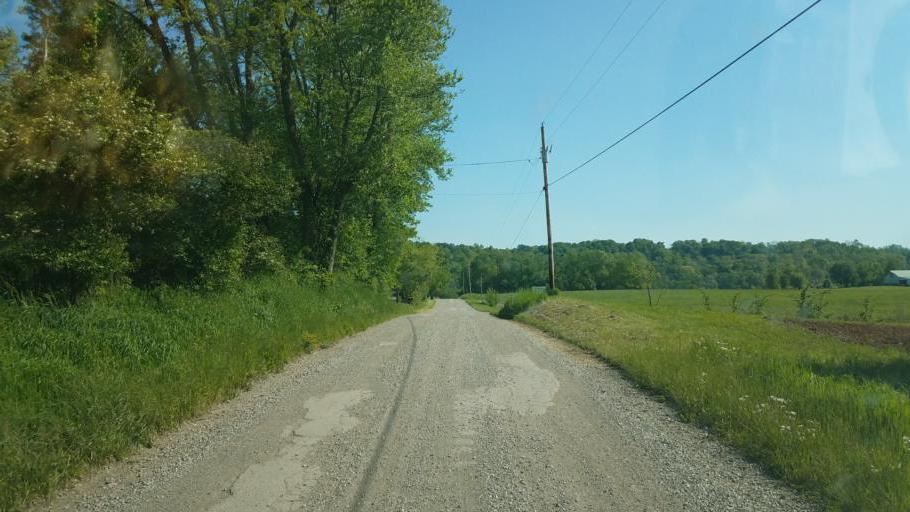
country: US
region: Ohio
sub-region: Belmont County
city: Barnesville
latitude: 40.0543
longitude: -81.3396
